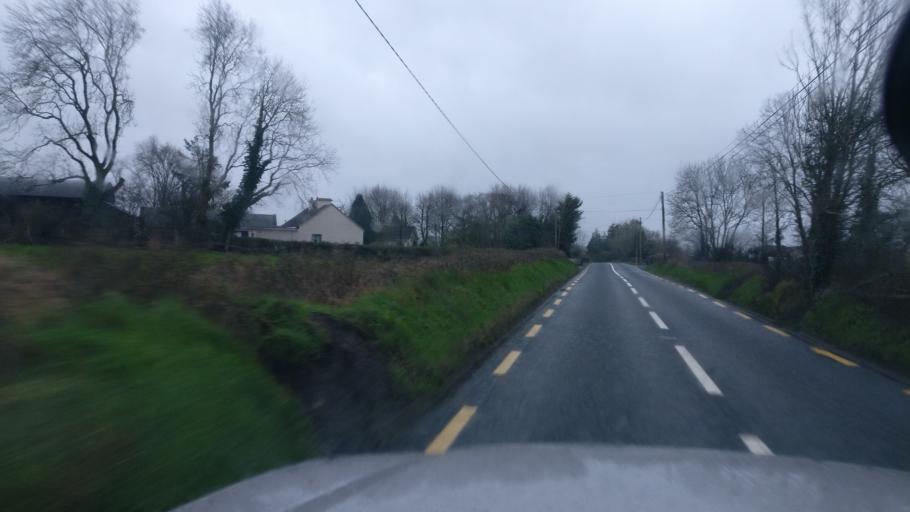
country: IE
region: Connaught
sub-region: County Galway
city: Portumna
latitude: 53.1294
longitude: -8.2090
